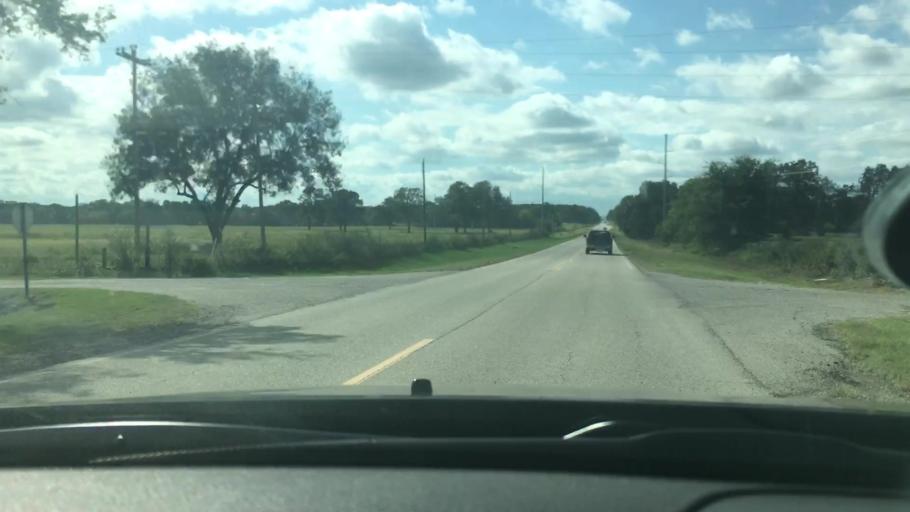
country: US
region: Oklahoma
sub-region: Pontotoc County
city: Ada
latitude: 34.7093
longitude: -96.6349
